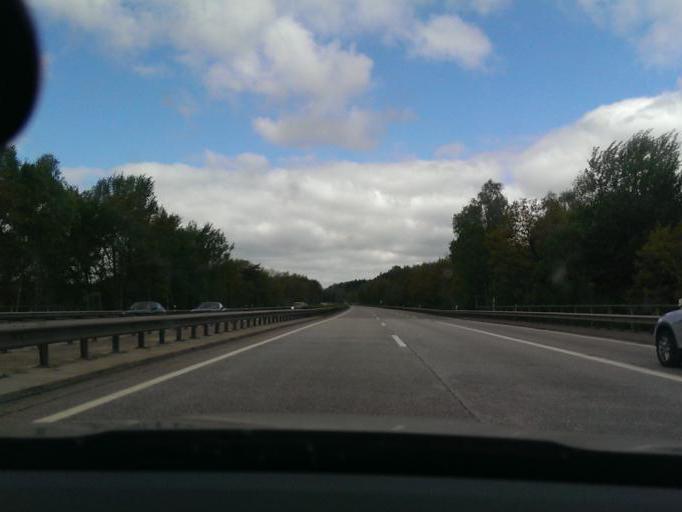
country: DE
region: Lower Saxony
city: Walsrode
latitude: 52.8372
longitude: 9.5919
